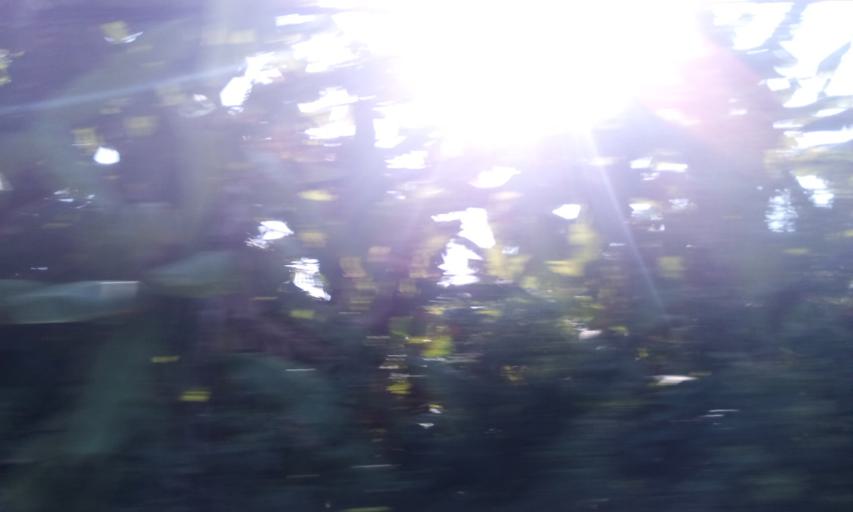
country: TH
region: Pathum Thani
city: Lam Luk Ka
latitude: 13.9462
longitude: 100.7059
